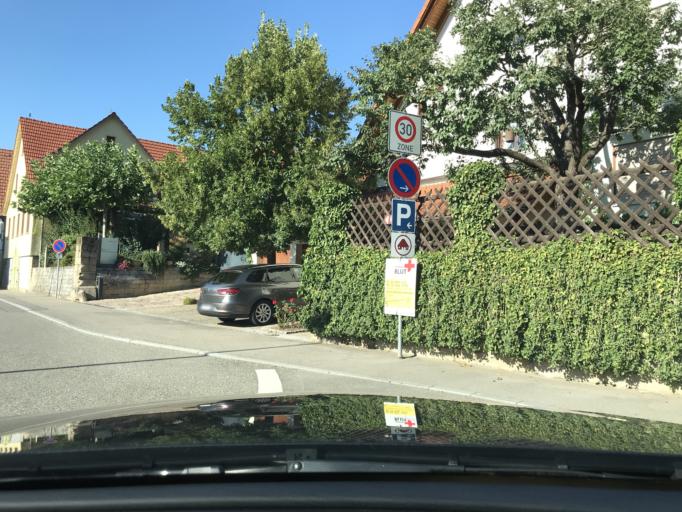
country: DE
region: Baden-Wuerttemberg
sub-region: Regierungsbezirk Stuttgart
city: Weinstadt-Endersbach
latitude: 48.7854
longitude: 9.3418
